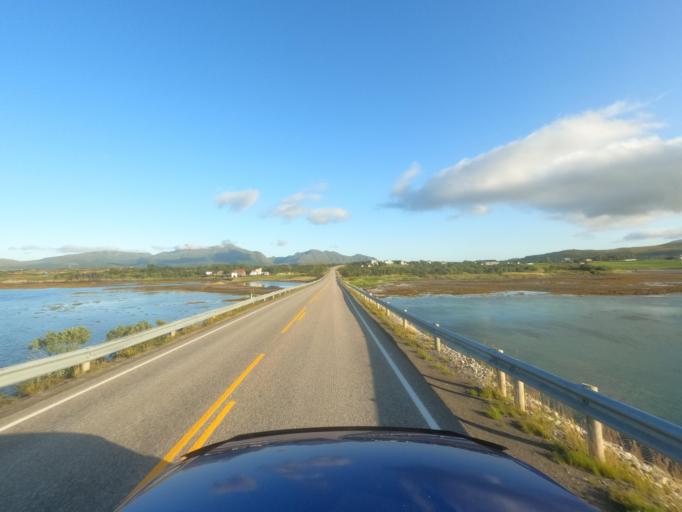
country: NO
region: Nordland
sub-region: Vestvagoy
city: Gravdal
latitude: 68.1543
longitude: 13.5341
